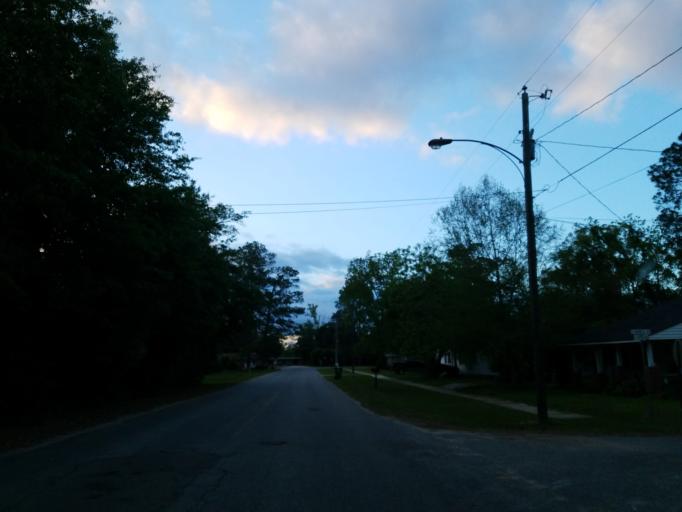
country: US
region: Georgia
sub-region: Cook County
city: Adel
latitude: 31.1468
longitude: -83.4258
